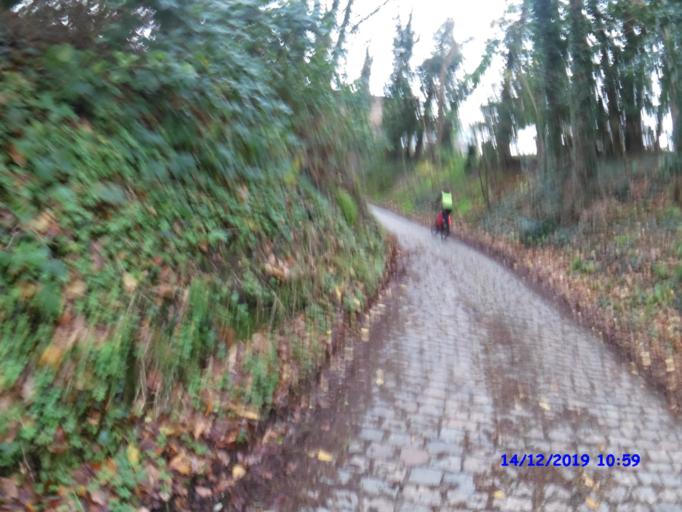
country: BE
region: Flanders
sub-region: Provincie Vlaams-Brabant
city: Beersel
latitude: 50.7593
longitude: 4.3001
